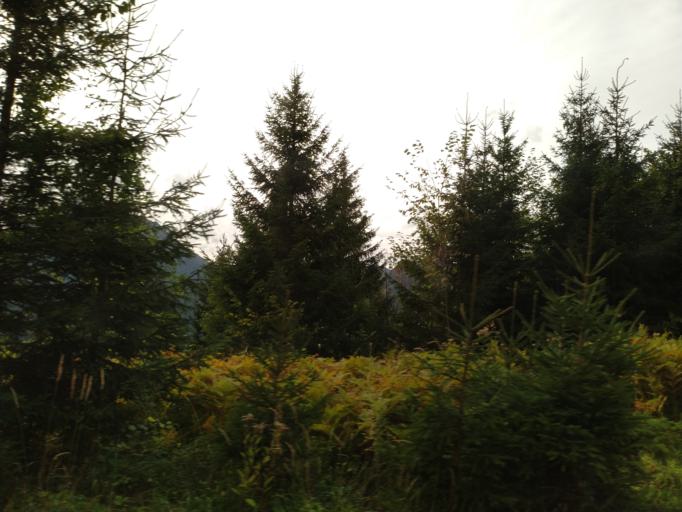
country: AT
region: Lower Austria
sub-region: Politischer Bezirk Scheibbs
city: Puchenstuben
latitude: 47.8795
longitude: 15.2987
